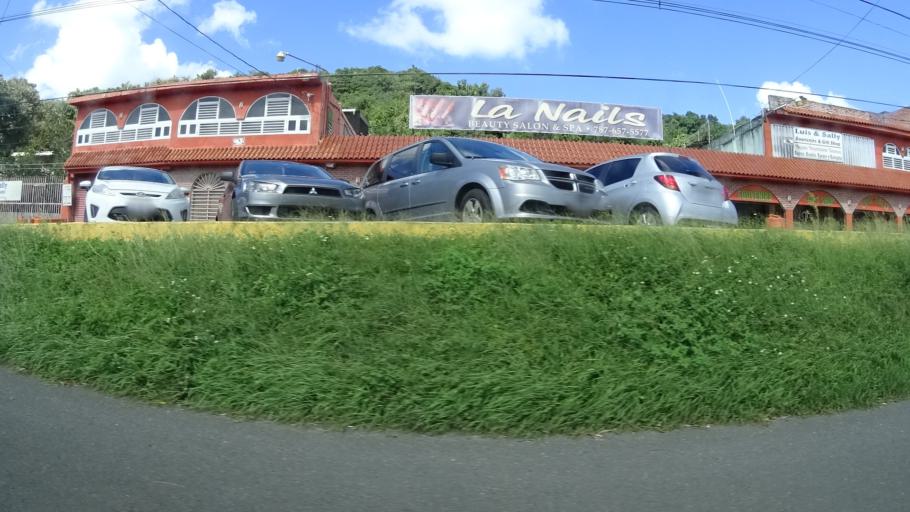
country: PR
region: Rio Grande
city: Palmer
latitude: 18.3721
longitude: -65.7714
